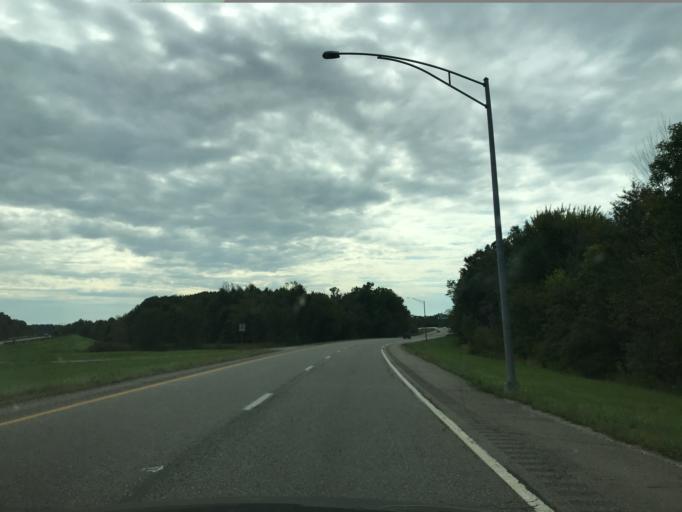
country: US
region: Ohio
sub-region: Trumbull County
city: Howland Center
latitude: 41.2426
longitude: -80.7634
